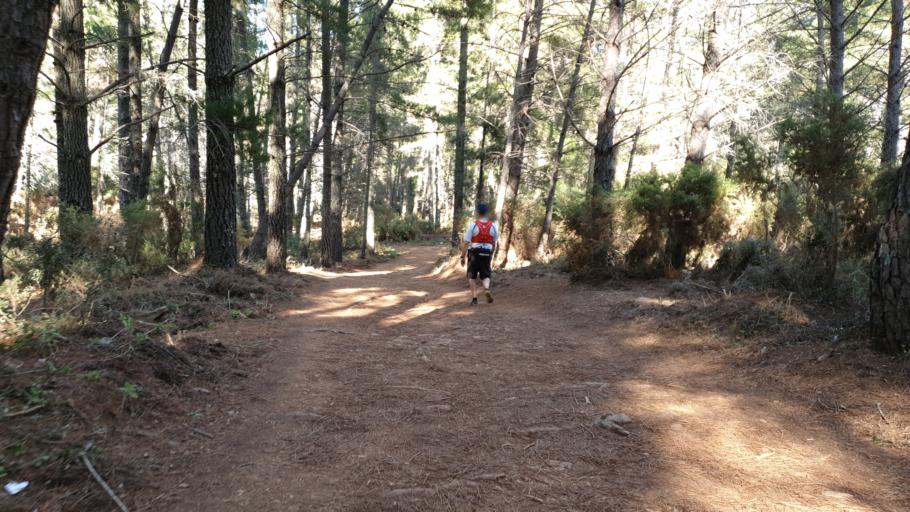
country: ES
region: Andalusia
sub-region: Provincia de Malaga
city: Ojen
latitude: 36.5724
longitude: -4.8944
